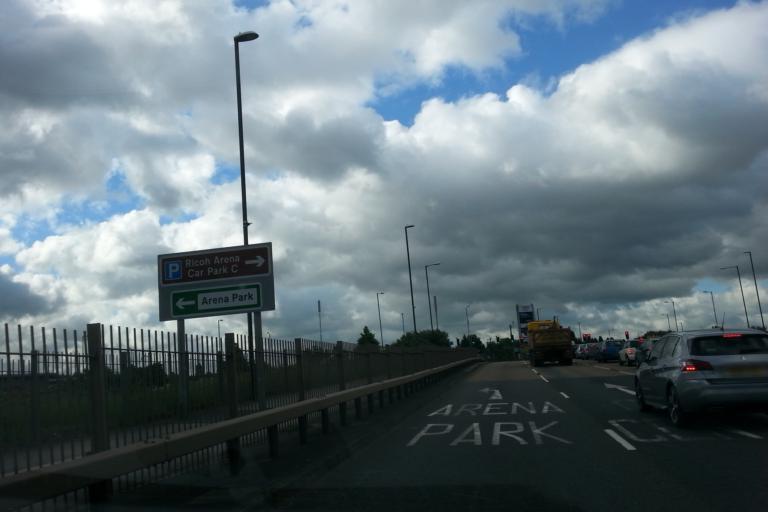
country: GB
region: England
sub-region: Warwickshire
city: Exhall
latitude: 52.4456
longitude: -1.4969
